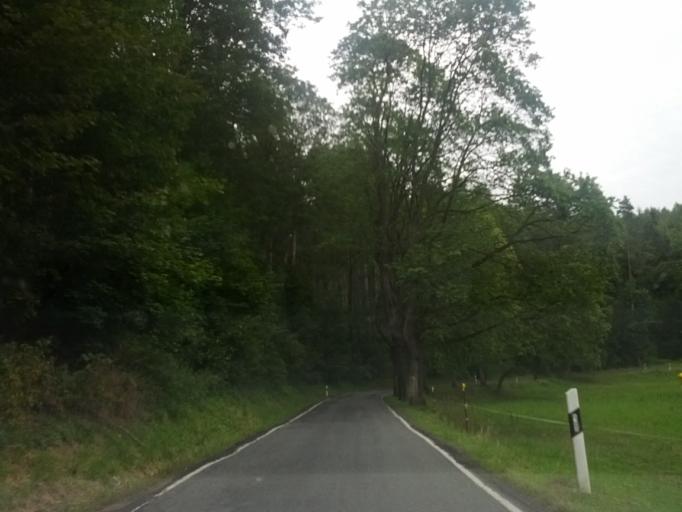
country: DE
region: Thuringia
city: Bad Salzungen
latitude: 50.8286
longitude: 10.2334
